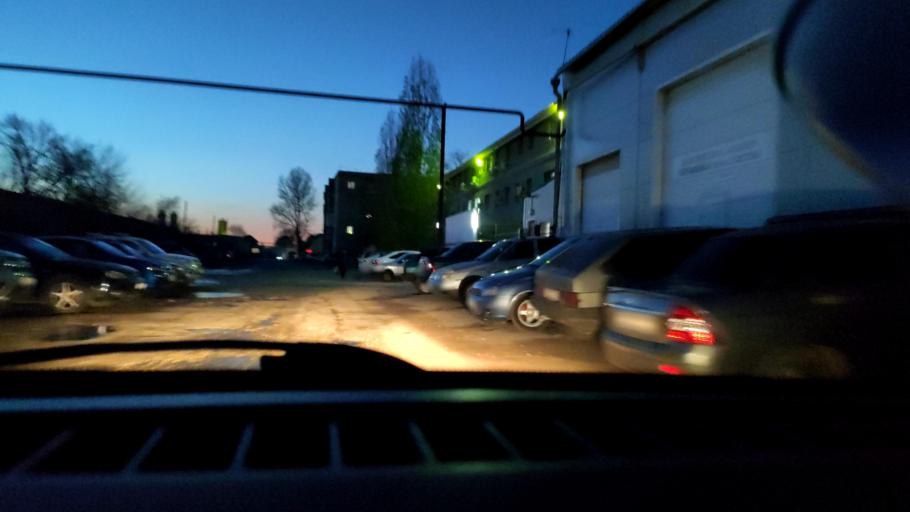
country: RU
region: Samara
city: Samara
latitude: 53.1294
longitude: 50.1070
